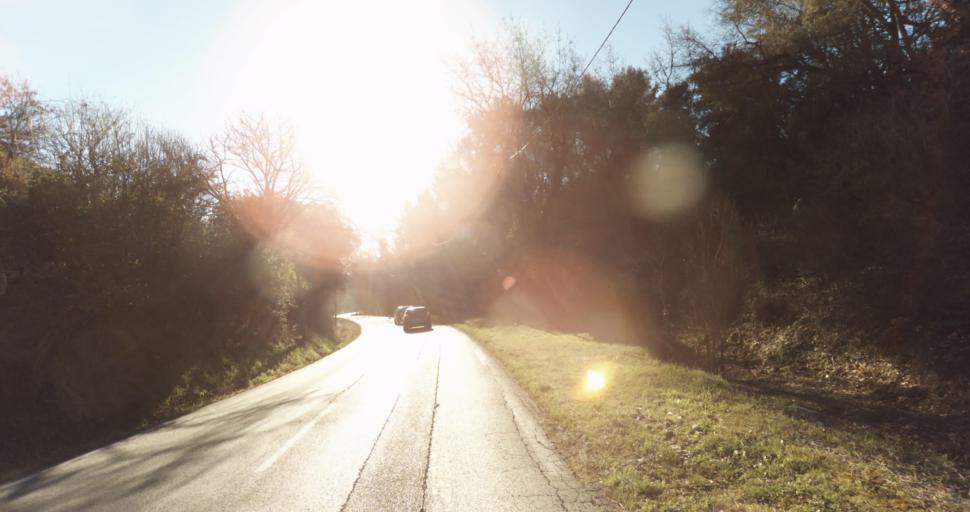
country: FR
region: Provence-Alpes-Cote d'Azur
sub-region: Departement des Bouches-du-Rhone
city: Cadolive
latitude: 43.4025
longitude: 5.5598
